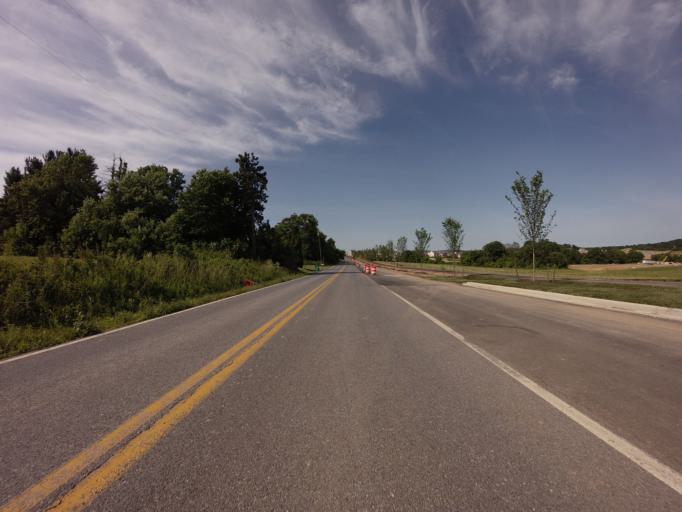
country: US
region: Maryland
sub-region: Frederick County
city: Green Valley
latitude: 39.3562
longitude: -77.2800
